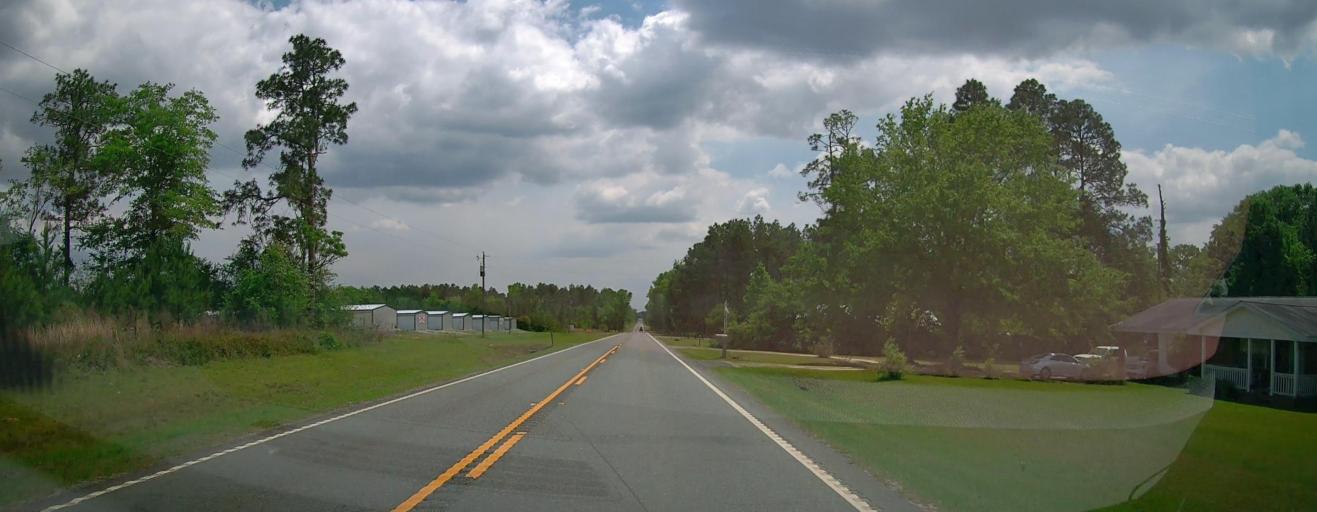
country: US
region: Georgia
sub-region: Treutlen County
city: Soperton
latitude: 32.4007
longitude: -82.6045
